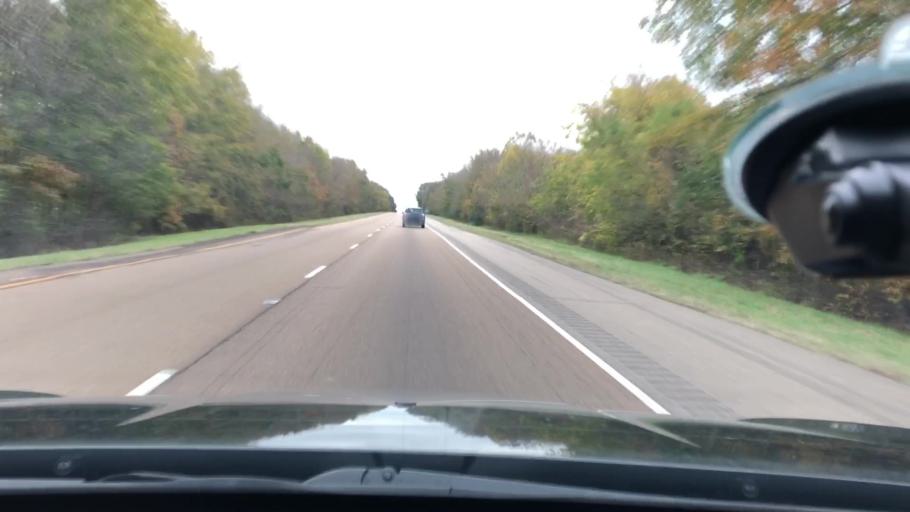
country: US
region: Arkansas
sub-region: Nevada County
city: Prescott
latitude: 33.7869
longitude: -93.4554
